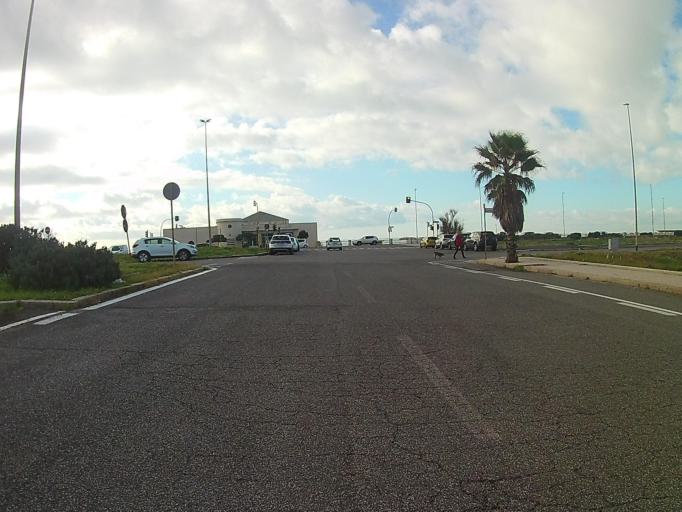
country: IT
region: Latium
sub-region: Citta metropolitana di Roma Capitale
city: Lido di Ostia
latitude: 41.7187
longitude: 12.3070
